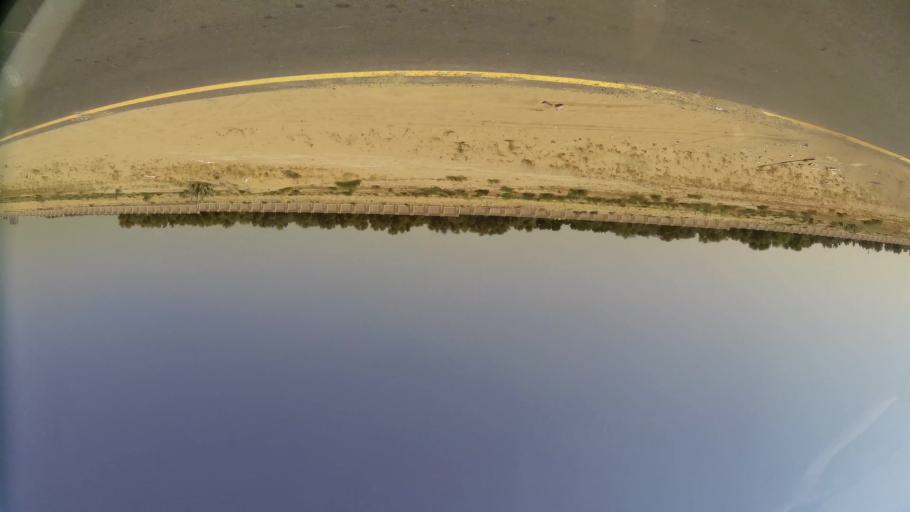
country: AE
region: Ajman
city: Ajman
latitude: 25.4034
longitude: 55.5344
